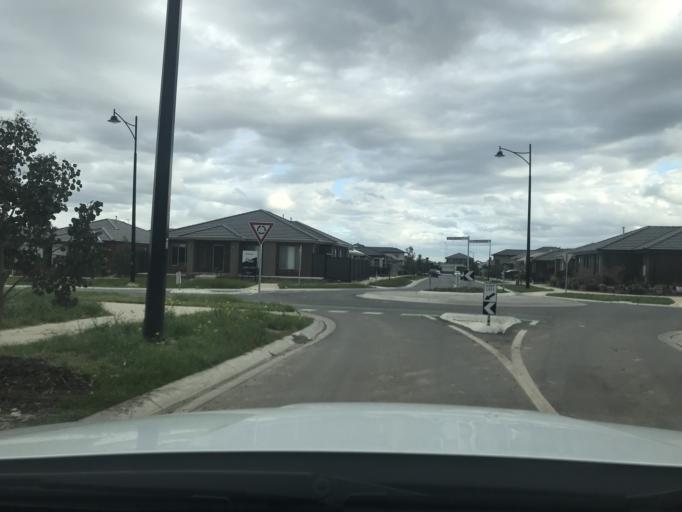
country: AU
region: Victoria
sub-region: Hume
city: Roxburgh Park
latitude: -37.5884
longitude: 144.8916
